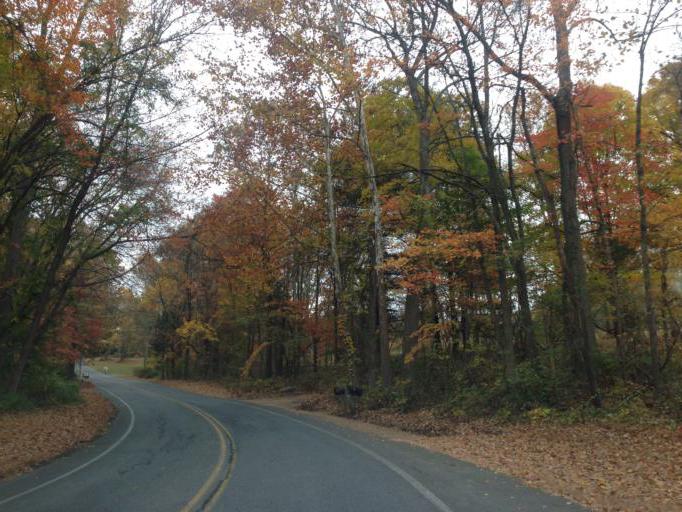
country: US
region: Maryland
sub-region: Carroll County
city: Sykesville
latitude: 39.2838
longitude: -76.9633
